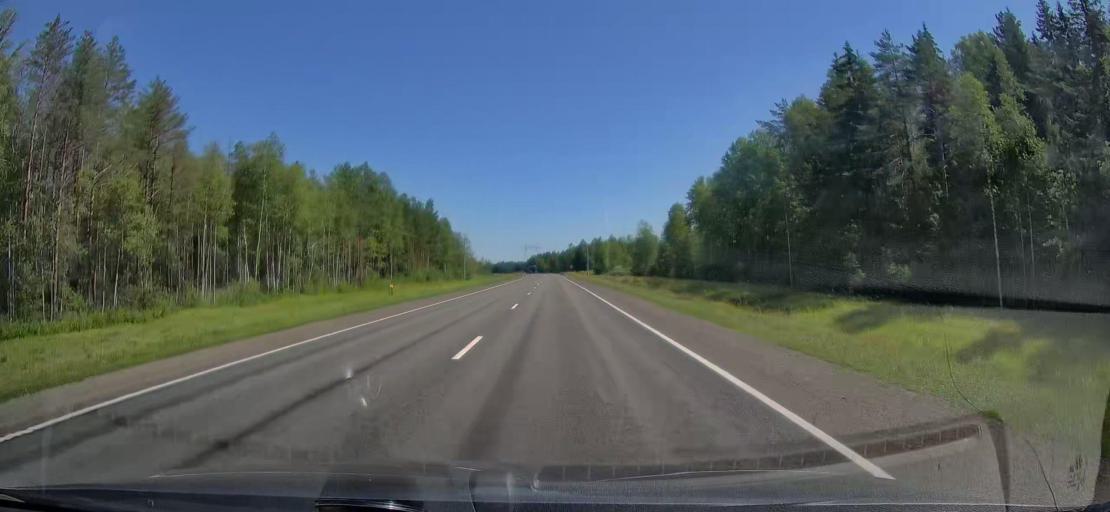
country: RU
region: Tverskaya
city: Ves'yegonsk
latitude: 58.9216
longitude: 37.2137
